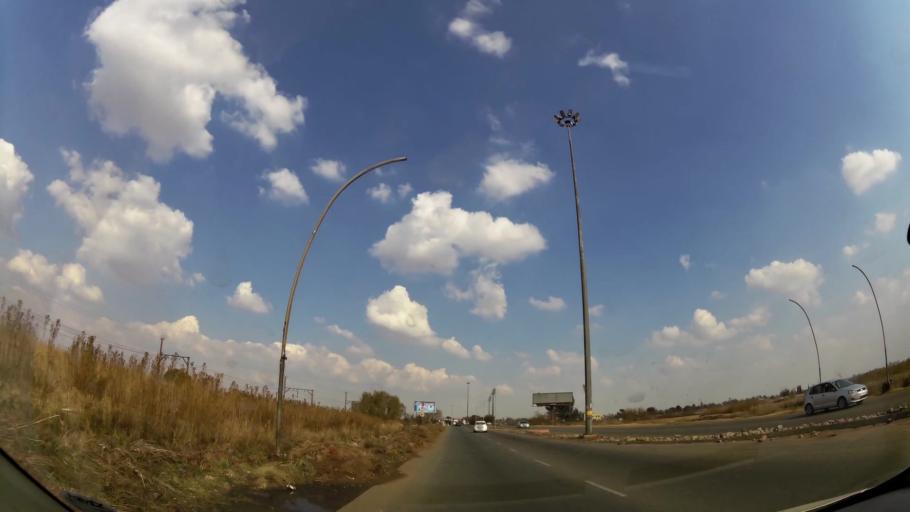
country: ZA
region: Gauteng
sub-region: Ekurhuleni Metropolitan Municipality
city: Germiston
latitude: -26.2987
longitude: 28.1601
